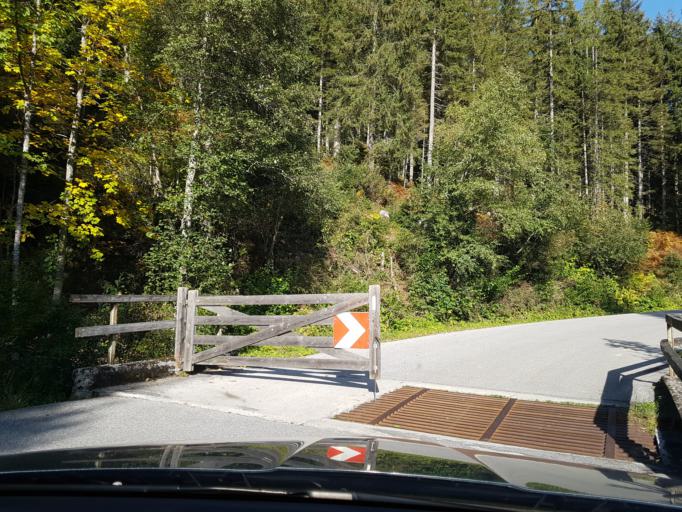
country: AT
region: Salzburg
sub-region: Politischer Bezirk Sankt Johann im Pongau
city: Filzmoos
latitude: 47.4060
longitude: 13.5010
